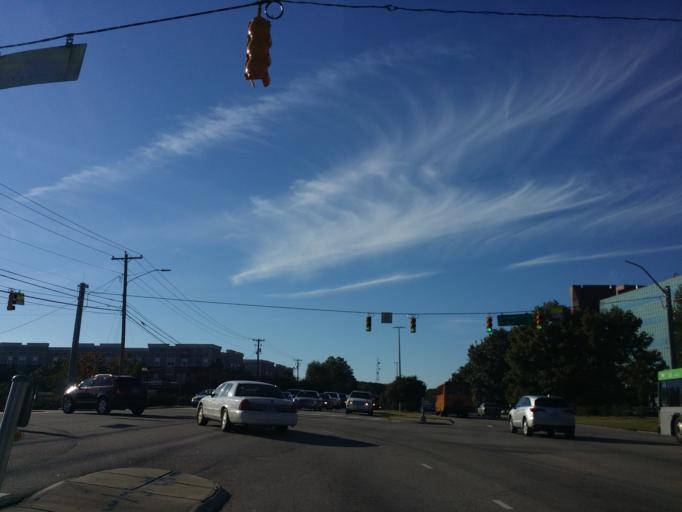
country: US
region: North Carolina
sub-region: Wake County
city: West Raleigh
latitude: 35.7807
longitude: -78.6752
